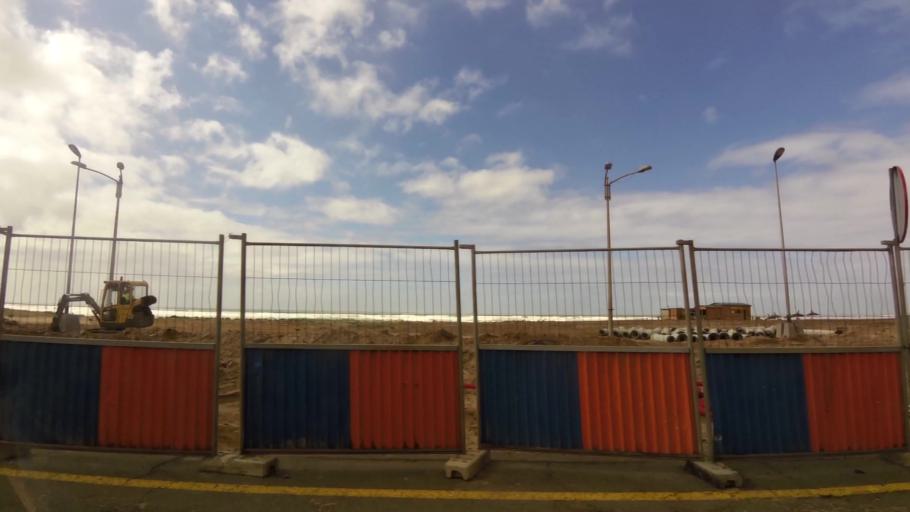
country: MA
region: Grand Casablanca
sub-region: Casablanca
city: Casablanca
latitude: 33.5831
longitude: -7.6931
